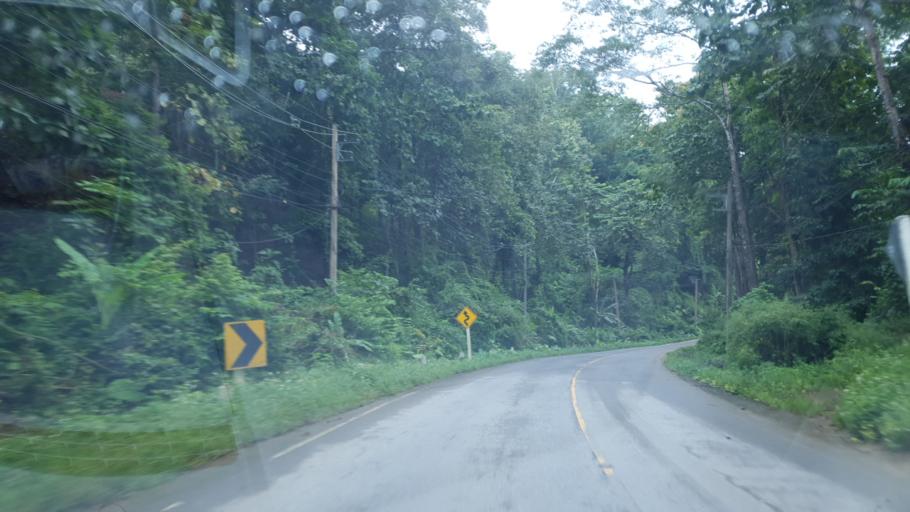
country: TH
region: Mae Hong Son
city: Ban Huai I Huak
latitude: 18.1463
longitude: 97.9739
